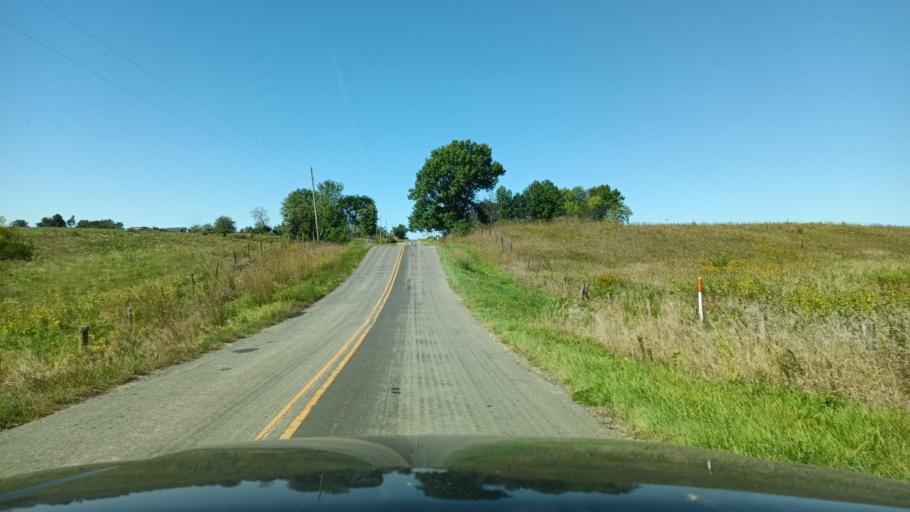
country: US
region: Missouri
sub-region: Scotland County
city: Memphis
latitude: 40.3538
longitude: -92.2947
